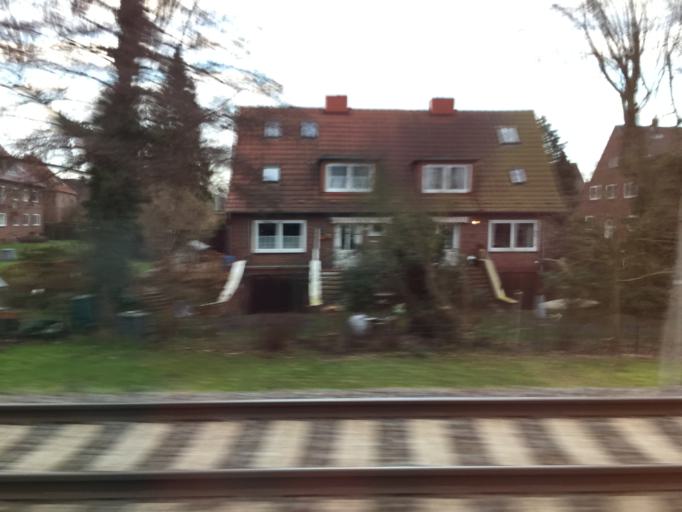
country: DE
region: Schleswig-Holstein
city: Gluckstadt
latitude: 53.7866
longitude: 9.4318
